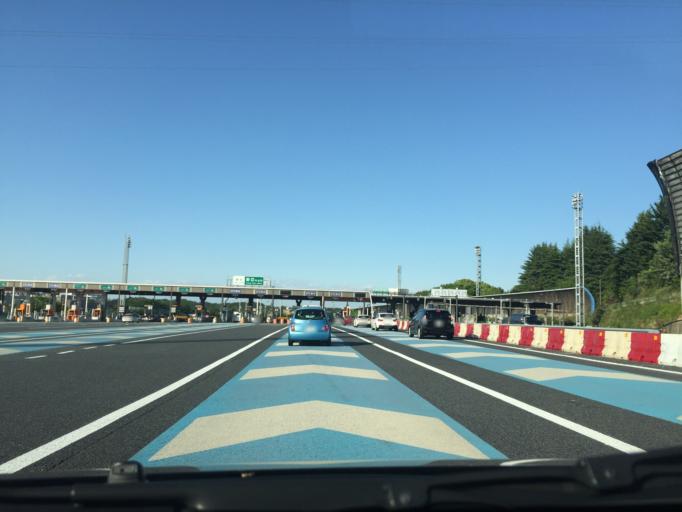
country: JP
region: Tokyo
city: Chofugaoka
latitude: 35.5933
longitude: 139.5723
